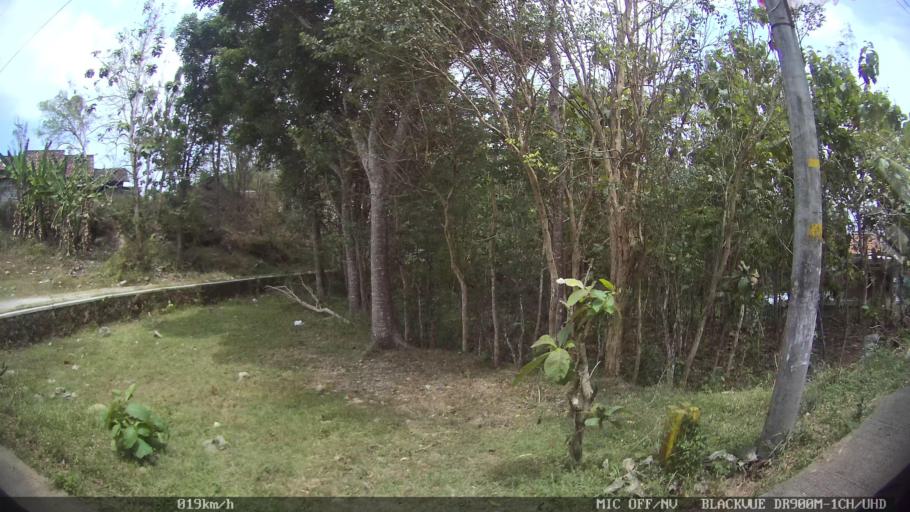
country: ID
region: Central Java
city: Candi Prambanan
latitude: -7.7886
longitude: 110.5176
